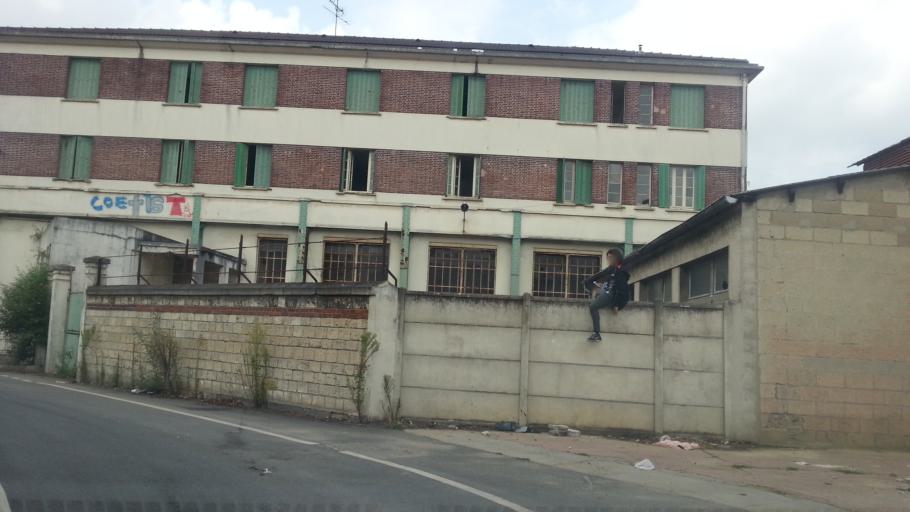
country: FR
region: Picardie
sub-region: Departement de l'Oise
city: Nogent-sur-Oise
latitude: 49.2592
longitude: 2.4619
